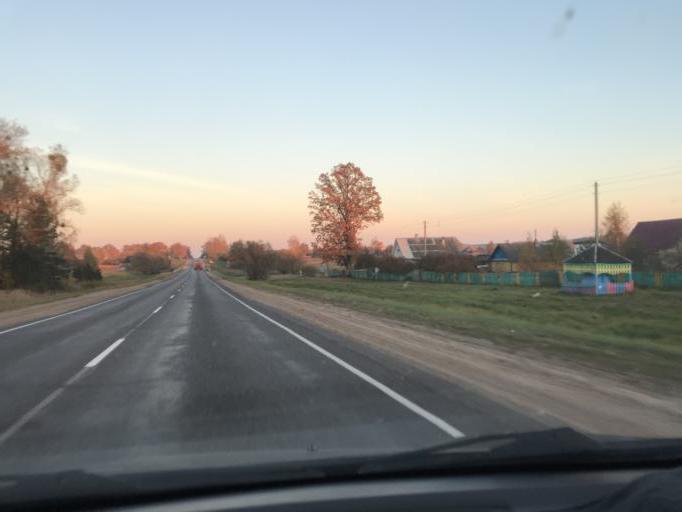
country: BY
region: Mogilev
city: Hlusha
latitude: 53.0924
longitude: 28.9297
